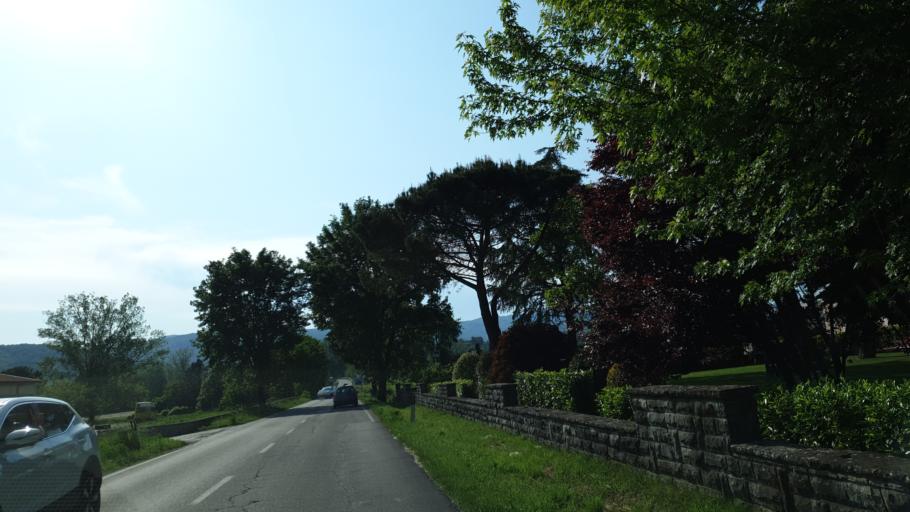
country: IT
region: Tuscany
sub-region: Province of Arezzo
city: Ponte a Poppi
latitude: 43.7393
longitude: 11.7457
